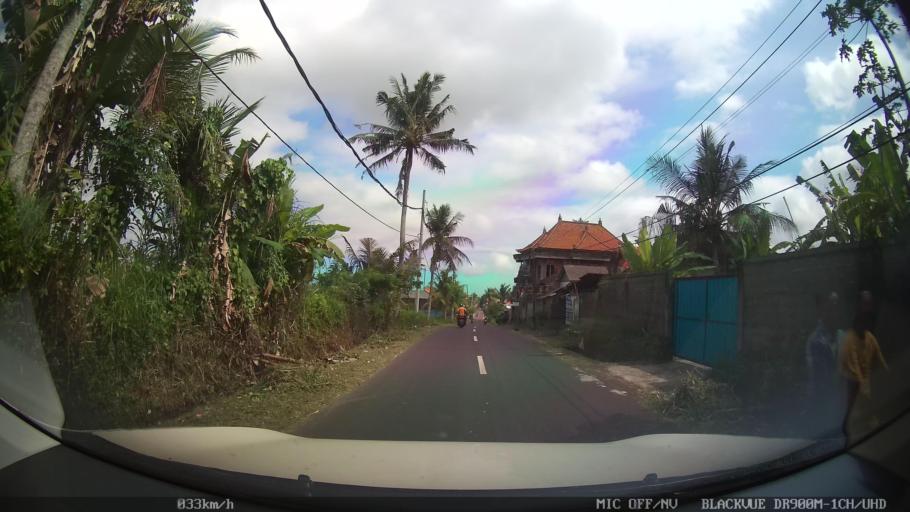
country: ID
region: Bali
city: Banjar Pesalakan
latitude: -8.5169
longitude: 115.3121
